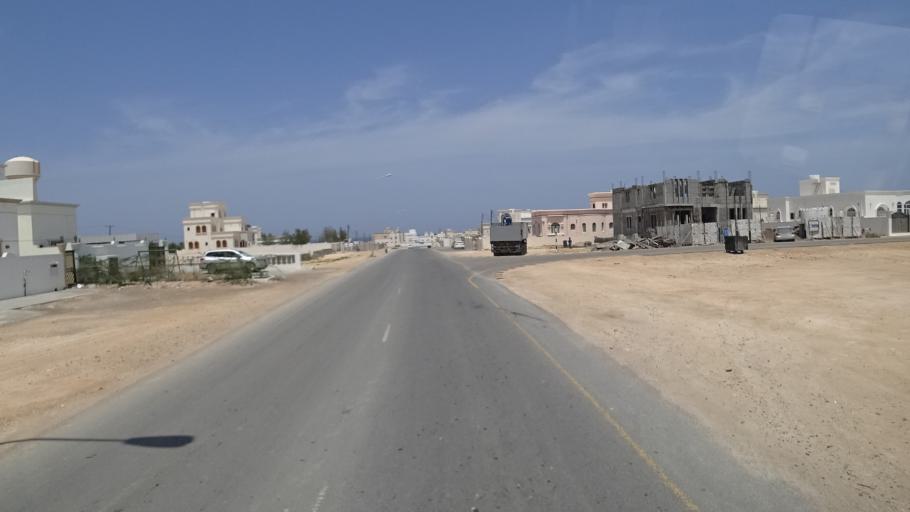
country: OM
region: Ash Sharqiyah
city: Sur
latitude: 22.6177
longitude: 59.4542
